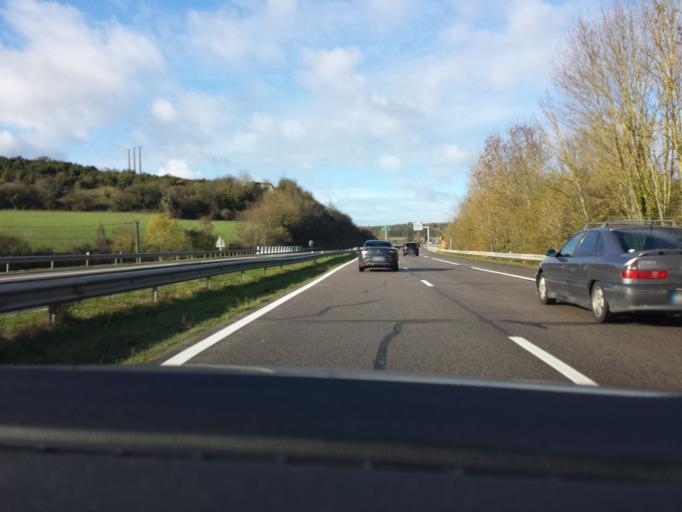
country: FR
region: Haute-Normandie
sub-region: Departement de l'Eure
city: Pacy-sur-Eure
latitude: 49.0090
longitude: 1.3625
